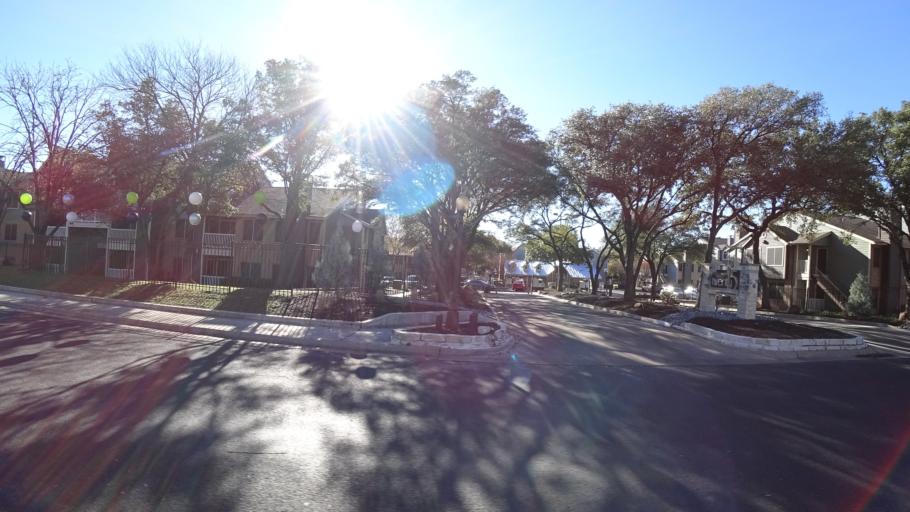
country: US
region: Texas
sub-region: Travis County
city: Wells Branch
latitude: 30.4094
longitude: -97.6992
